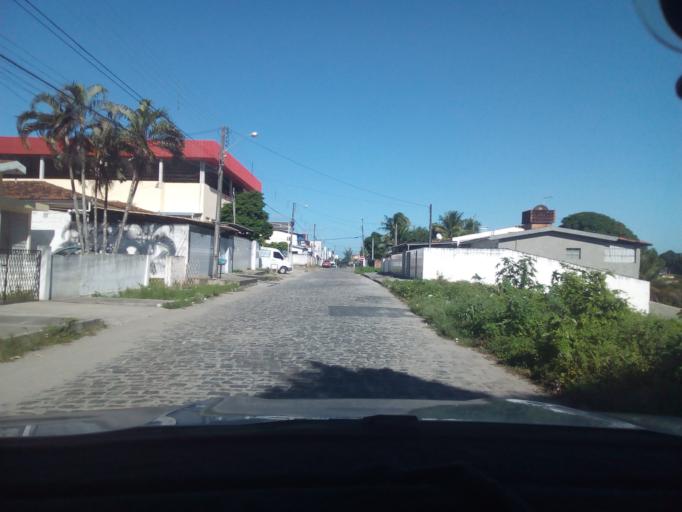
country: BR
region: Paraiba
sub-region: Joao Pessoa
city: Joao Pessoa
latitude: -7.1544
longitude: -34.8802
